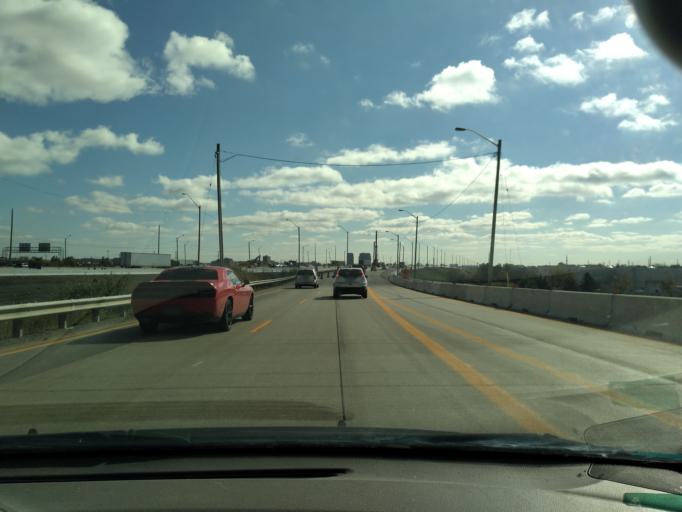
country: CA
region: Ontario
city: Etobicoke
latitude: 43.7504
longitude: -79.6319
